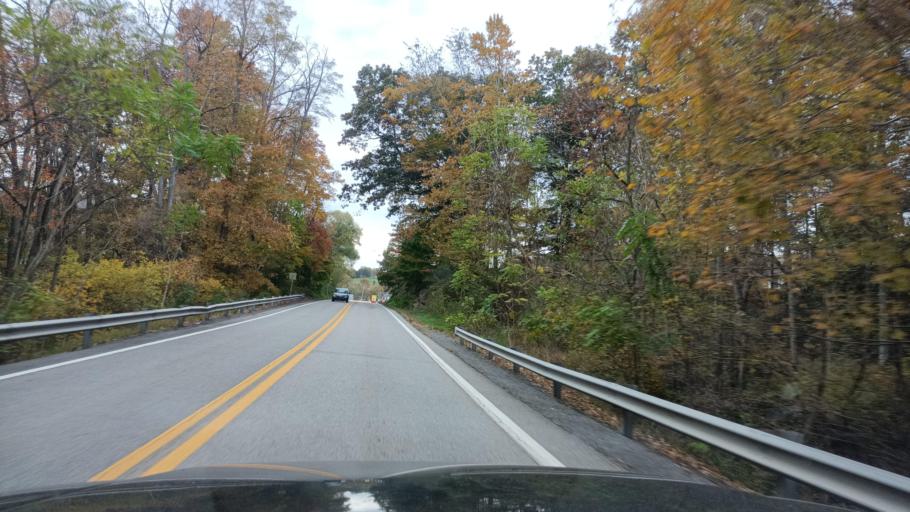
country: US
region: West Virginia
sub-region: Taylor County
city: Grafton
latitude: 39.3453
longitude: -80.0006
